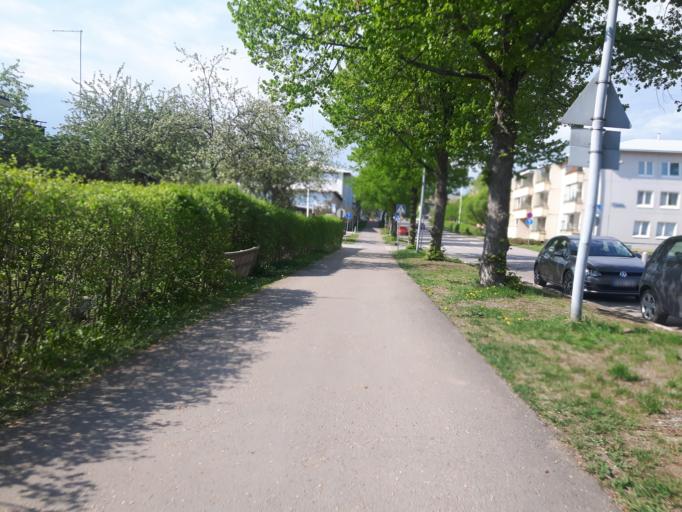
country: FI
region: Uusimaa
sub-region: Porvoo
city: Porvoo
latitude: 60.3951
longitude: 25.6730
